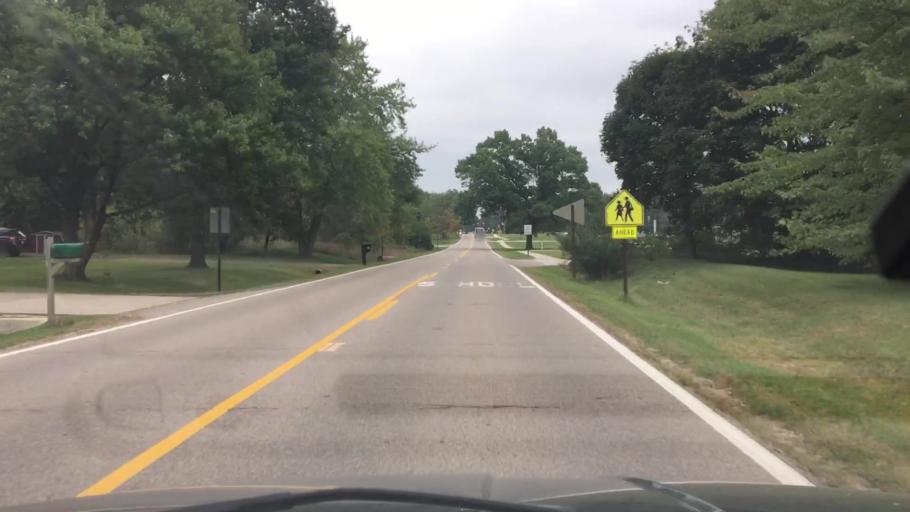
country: US
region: Michigan
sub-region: Livingston County
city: Brighton
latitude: 42.5075
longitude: -83.7743
